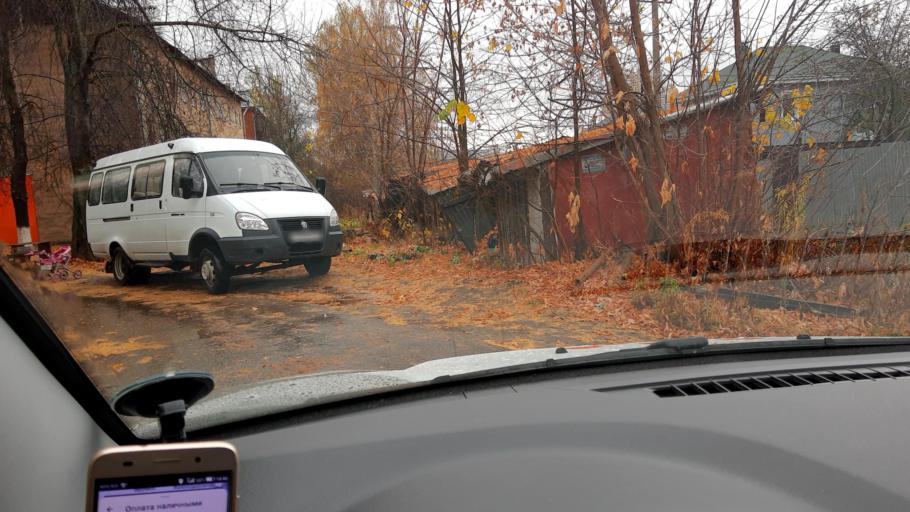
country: RU
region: Nizjnij Novgorod
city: Nizhniy Novgorod
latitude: 56.2622
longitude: 43.9900
